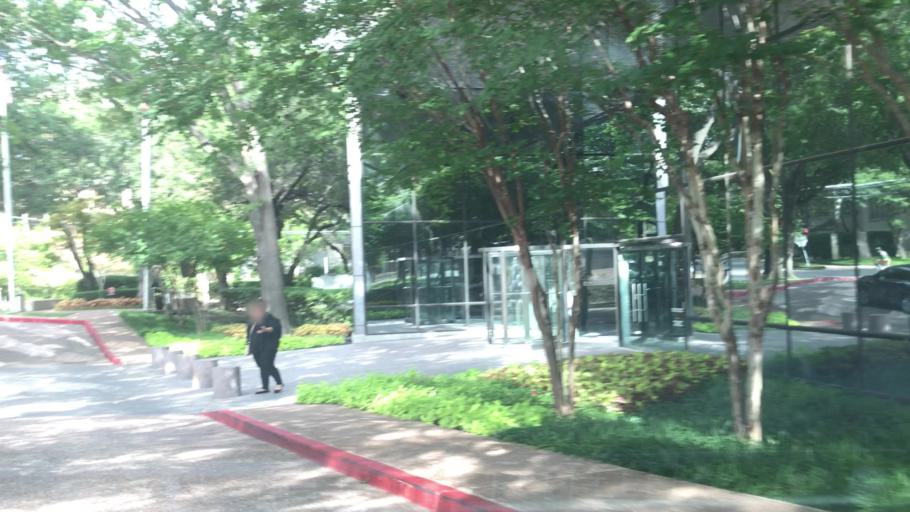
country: US
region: Texas
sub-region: Dallas County
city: Dallas
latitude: 32.8028
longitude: -96.8123
